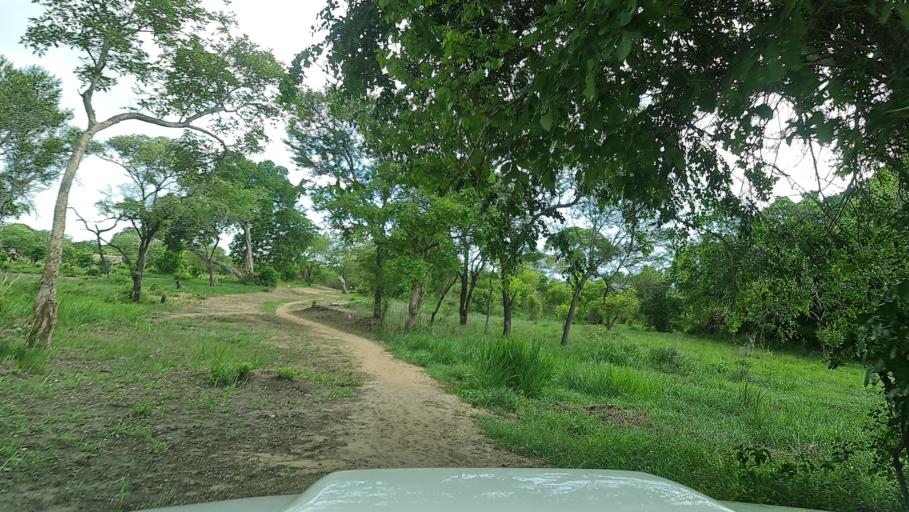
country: MZ
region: Nampula
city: Ilha de Mocambique
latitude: -15.5007
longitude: 40.1585
